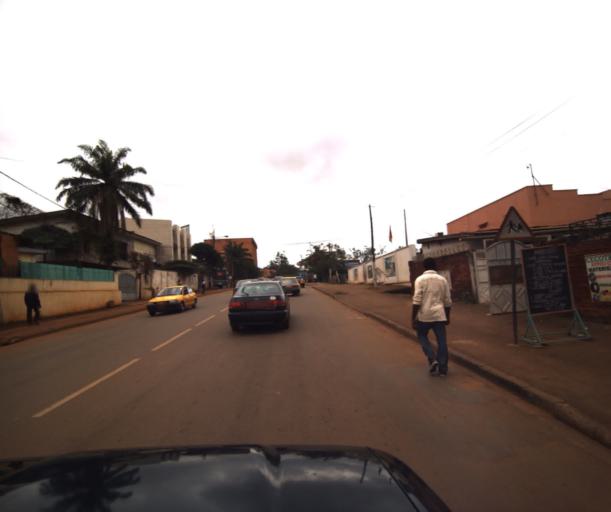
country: CM
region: Centre
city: Yaounde
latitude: 3.8377
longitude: 11.5159
